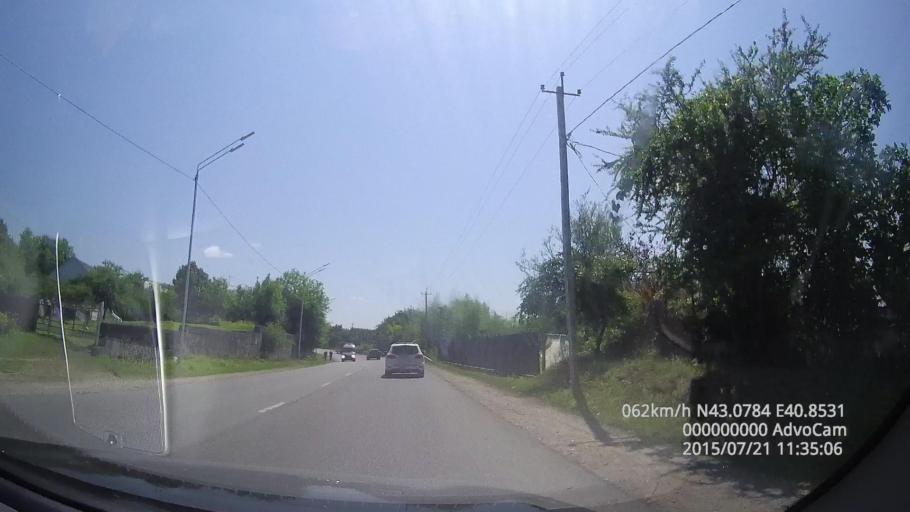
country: GE
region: Abkhazia
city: Stantsiya Novyy Afon
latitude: 43.0783
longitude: 40.8537
